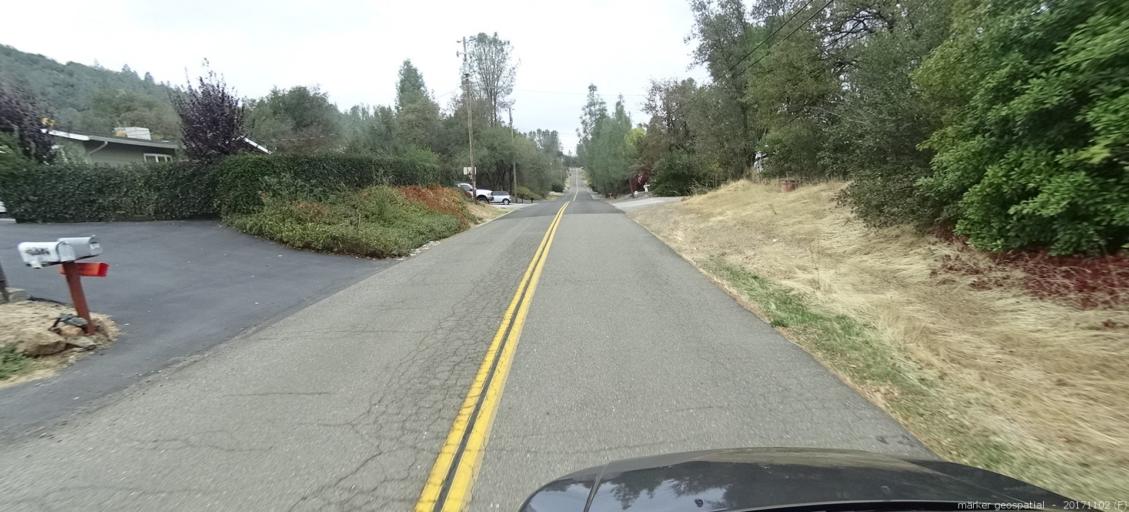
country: US
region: California
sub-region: Shasta County
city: Central Valley (historical)
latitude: 40.6545
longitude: -122.3977
